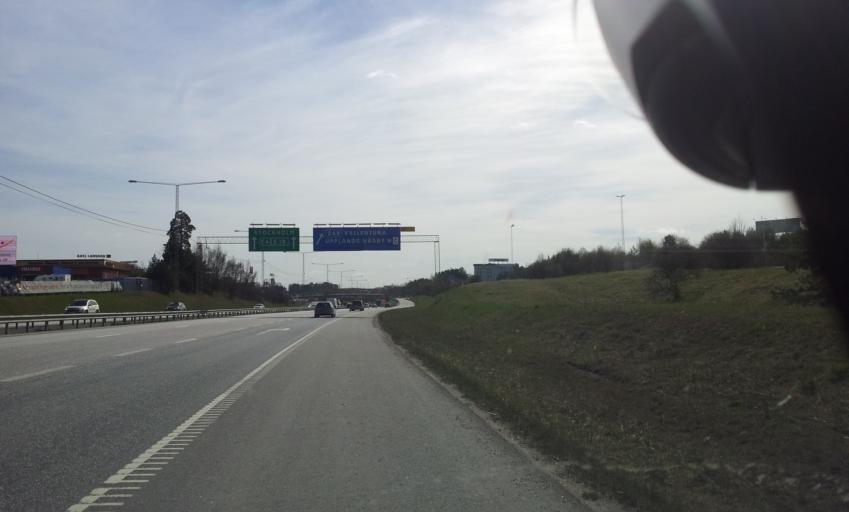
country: SE
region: Stockholm
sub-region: Upplands Vasby Kommun
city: Upplands Vaesby
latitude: 59.5206
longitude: 17.9261
